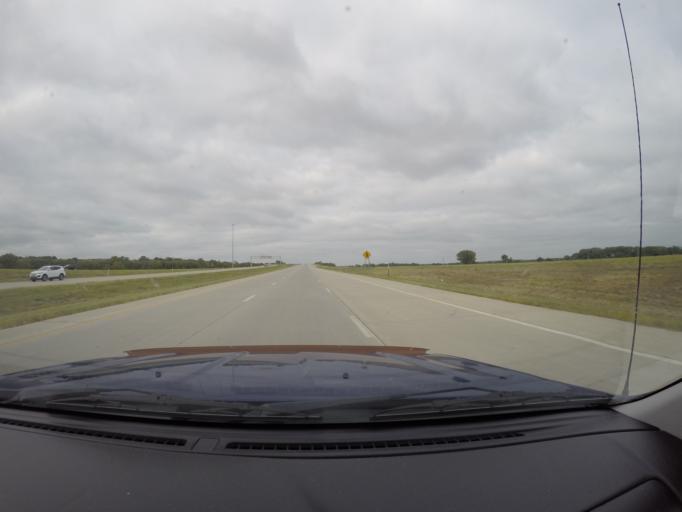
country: US
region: Kansas
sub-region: Riley County
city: Ogden
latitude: 39.1156
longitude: -96.6948
